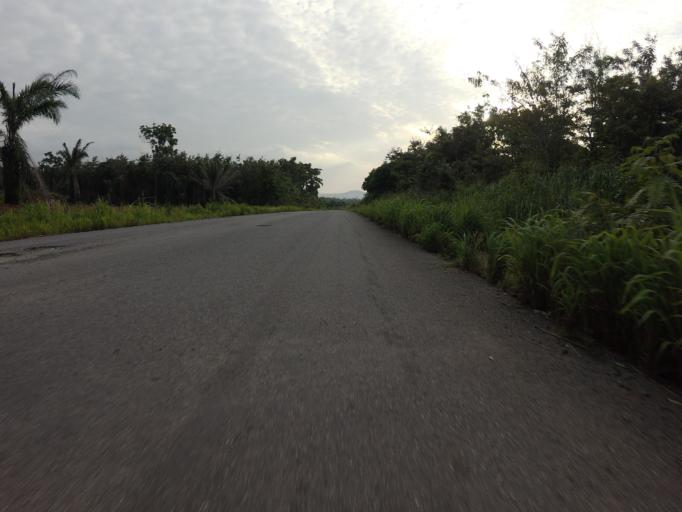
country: GH
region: Volta
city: Kpandu
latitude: 6.8675
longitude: 0.4093
